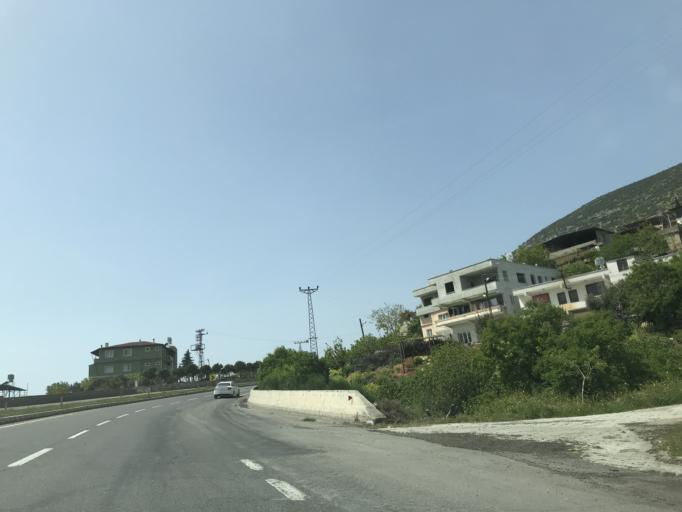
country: TR
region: Hatay
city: Belen
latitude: 36.4834
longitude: 36.2710
